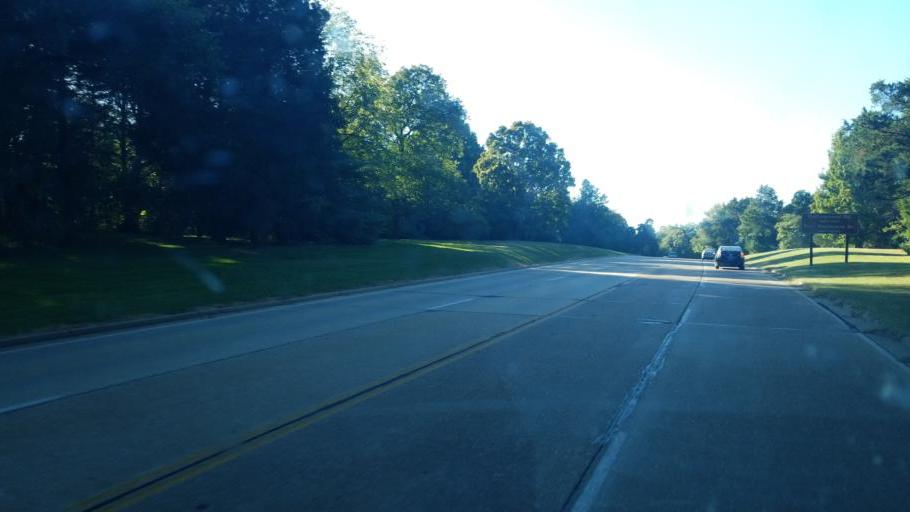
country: US
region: Virginia
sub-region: Fairfax County
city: Fort Hunt
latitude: 38.7303
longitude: -77.0442
